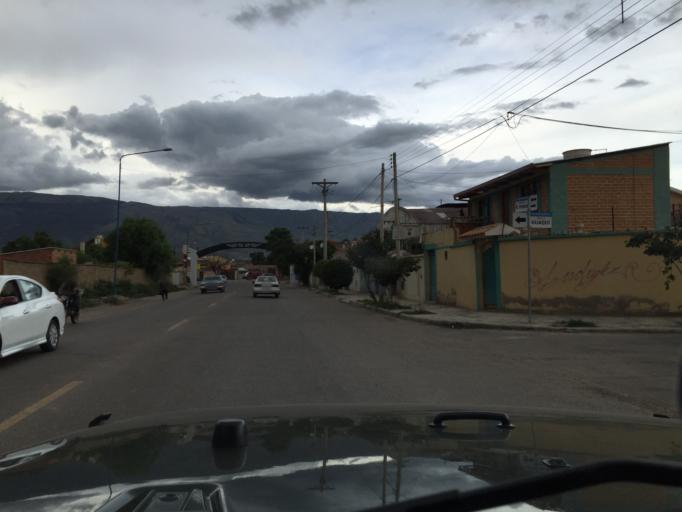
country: BO
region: Cochabamba
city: Cochabamba
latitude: -17.4114
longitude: -66.1678
